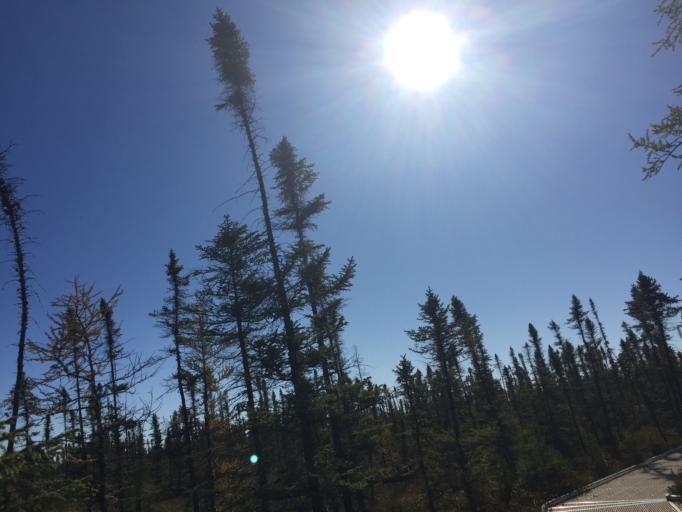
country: US
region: Minnesota
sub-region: Lake of the Woods County
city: Baudette
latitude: 48.2976
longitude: -94.5671
